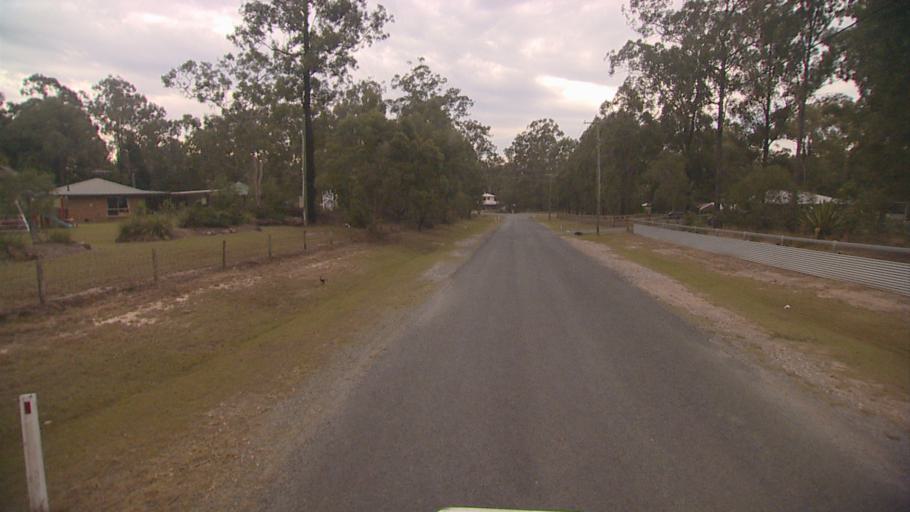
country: AU
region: Queensland
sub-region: Logan
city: Chambers Flat
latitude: -27.7938
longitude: 153.1162
